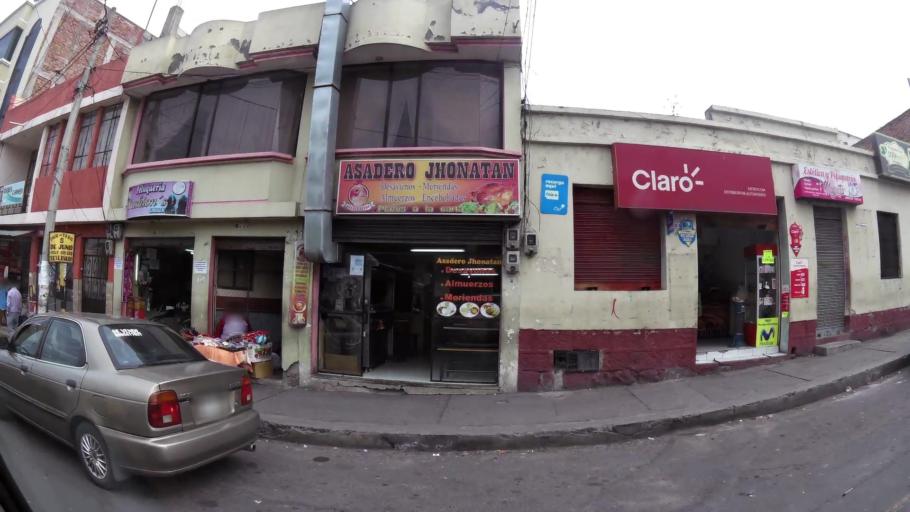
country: EC
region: Cotopaxi
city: Latacunga
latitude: -0.9330
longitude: -78.6217
